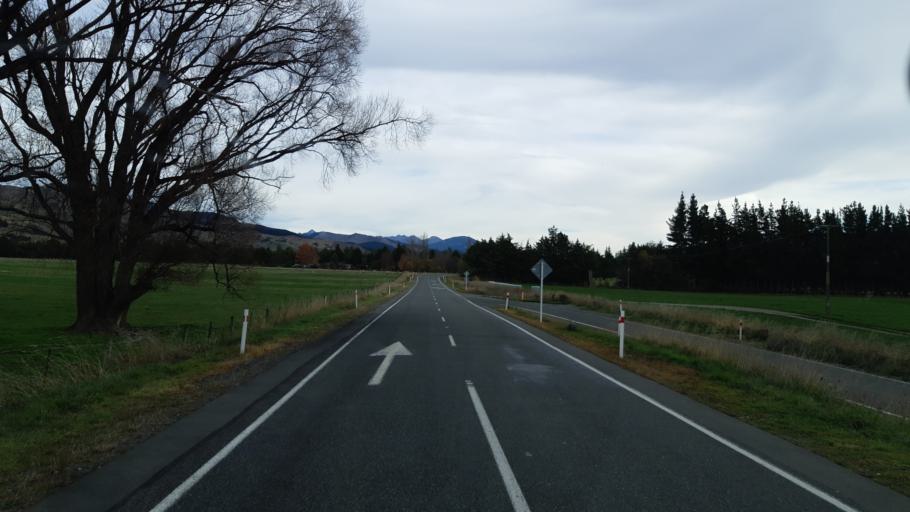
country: NZ
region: Tasman
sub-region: Tasman District
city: Brightwater
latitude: -41.6359
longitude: 173.3228
